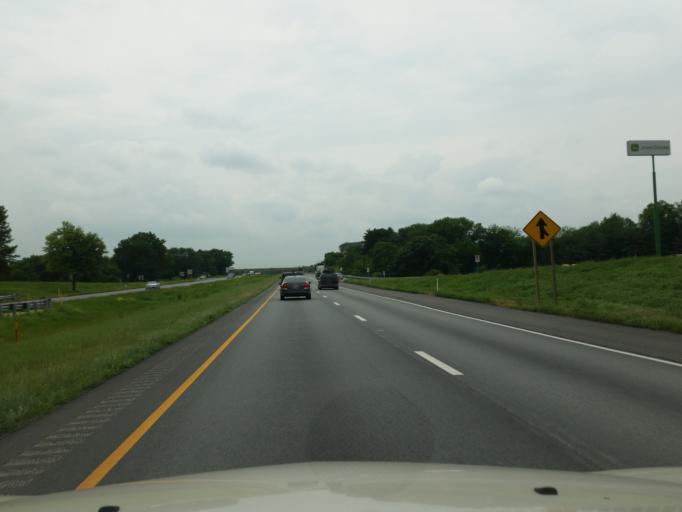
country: US
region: Pennsylvania
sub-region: Lancaster County
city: Mount Joy
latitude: 40.1247
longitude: -76.4692
